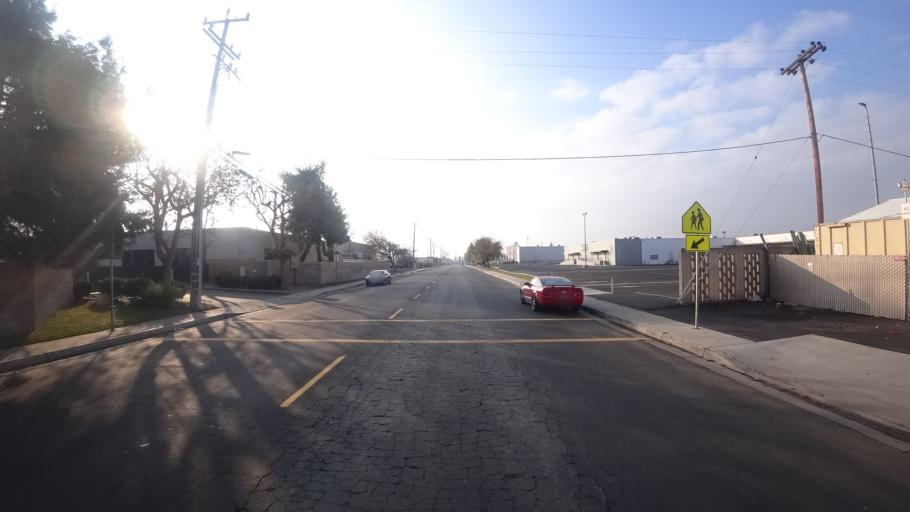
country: US
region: California
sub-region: Kern County
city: Bakersfield
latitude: 35.3169
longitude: -119.0584
